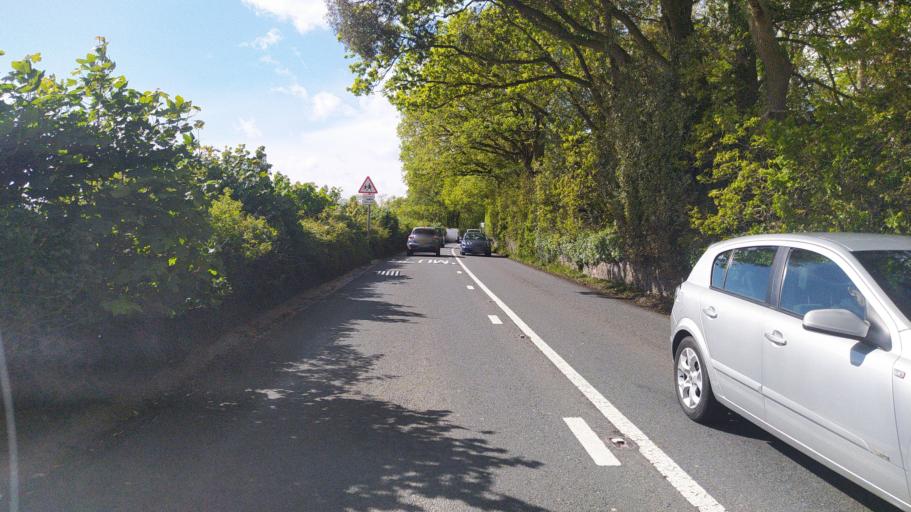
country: GB
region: England
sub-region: Devon
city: Newton Abbot
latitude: 50.5522
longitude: -3.6415
